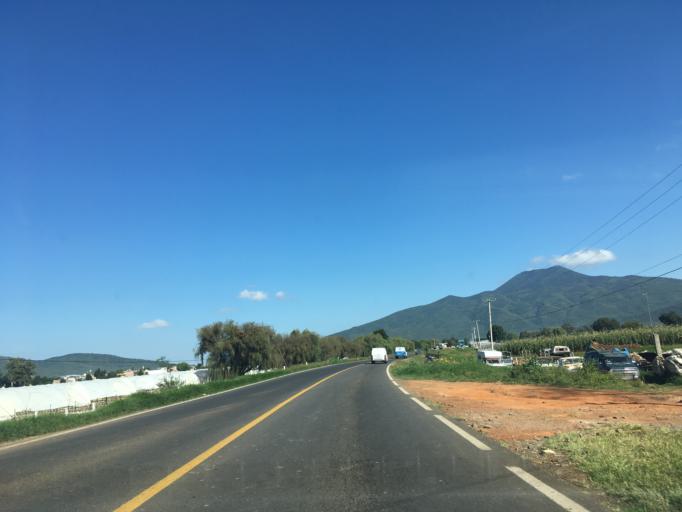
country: MX
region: Mexico
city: Tangancicuaro de Arista
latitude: 19.8739
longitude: -102.1976
